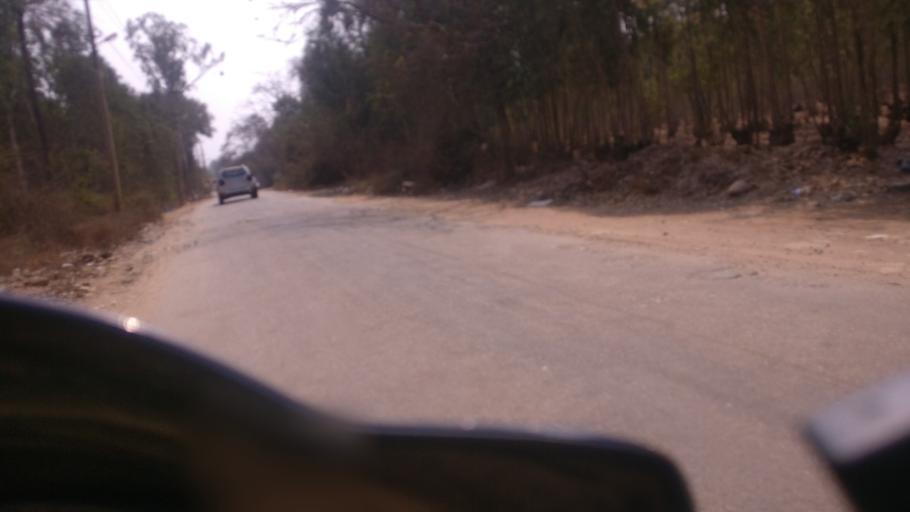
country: IN
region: Karnataka
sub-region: Bangalore Urban
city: Bangalore
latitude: 12.8995
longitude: 77.6852
